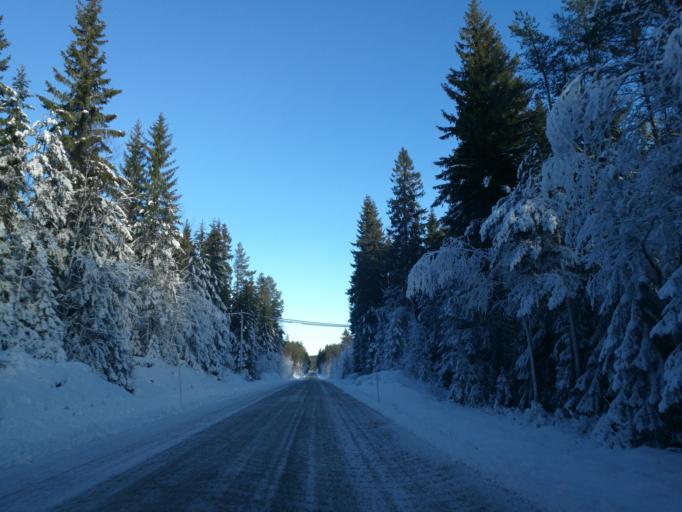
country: NO
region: Hedmark
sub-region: Grue
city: Kirkenaer
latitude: 60.4761
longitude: 12.5559
